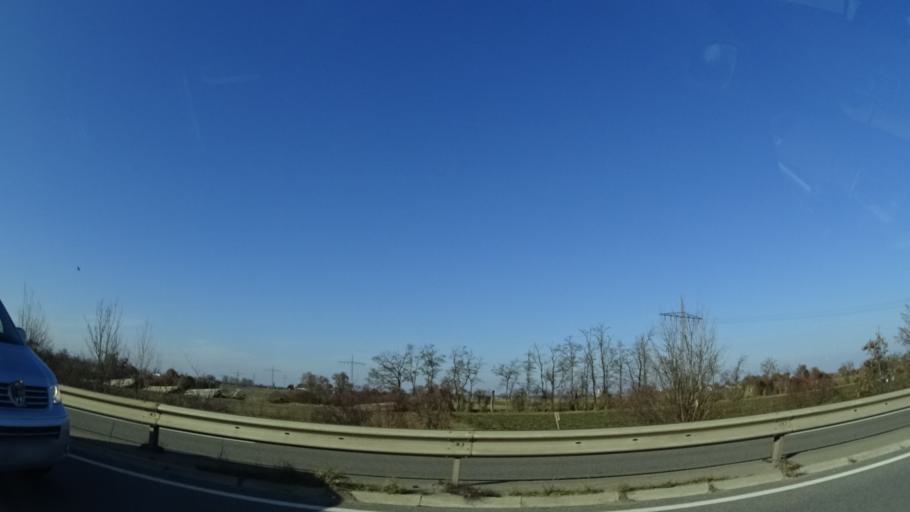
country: DE
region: Rheinland-Pfalz
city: Mutterstadt
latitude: 49.4820
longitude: 8.3390
